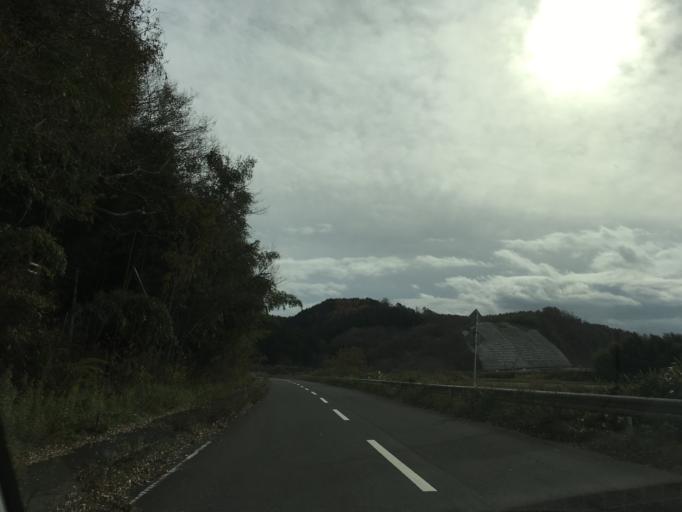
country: JP
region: Iwate
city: Ichinoseki
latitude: 38.7547
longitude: 141.2837
